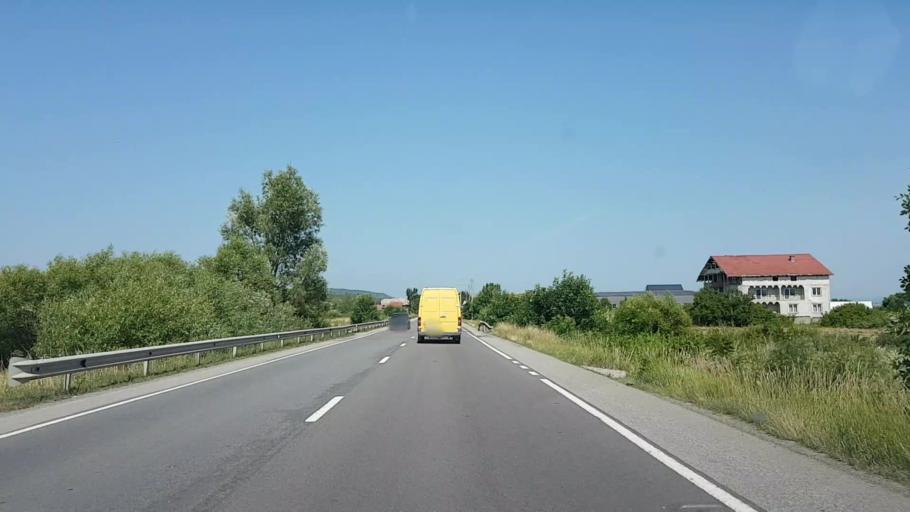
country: RO
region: Bistrita-Nasaud
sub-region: Comuna Ciceu-Mihaiesti
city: Ciceu-Mihaiesti
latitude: 47.1797
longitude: 23.9537
